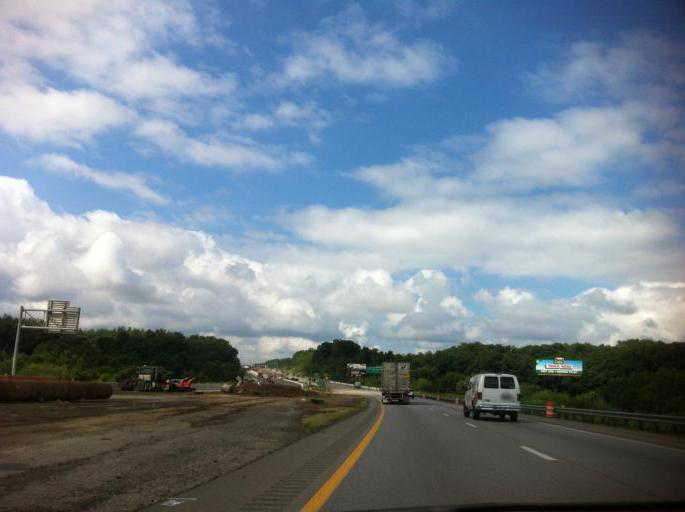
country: US
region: Ohio
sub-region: Trumbull County
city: Girard
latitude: 41.1481
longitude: -80.7067
